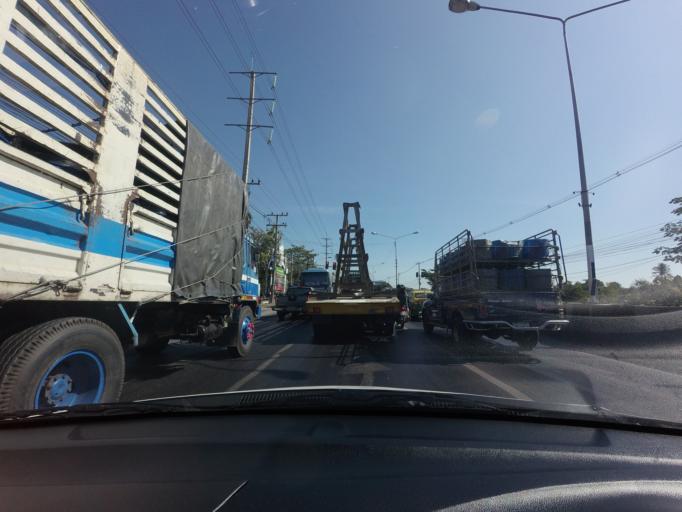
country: TH
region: Pathum Thani
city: Thanyaburi
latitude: 14.0201
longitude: 100.7343
